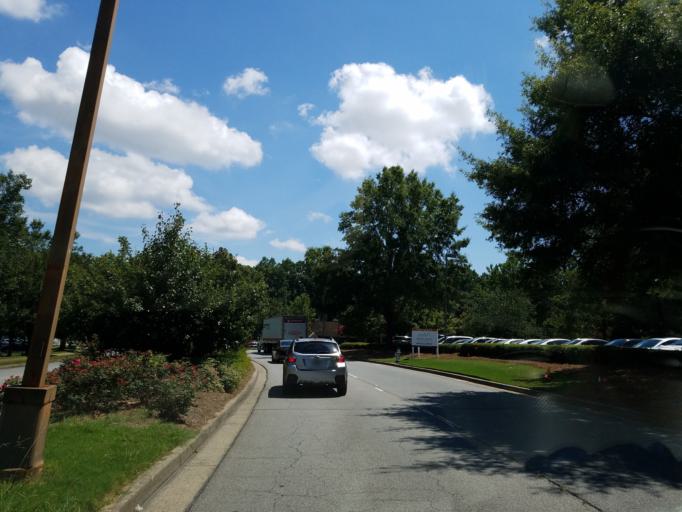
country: US
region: Georgia
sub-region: Fulton County
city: Alpharetta
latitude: 34.0829
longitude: -84.2737
